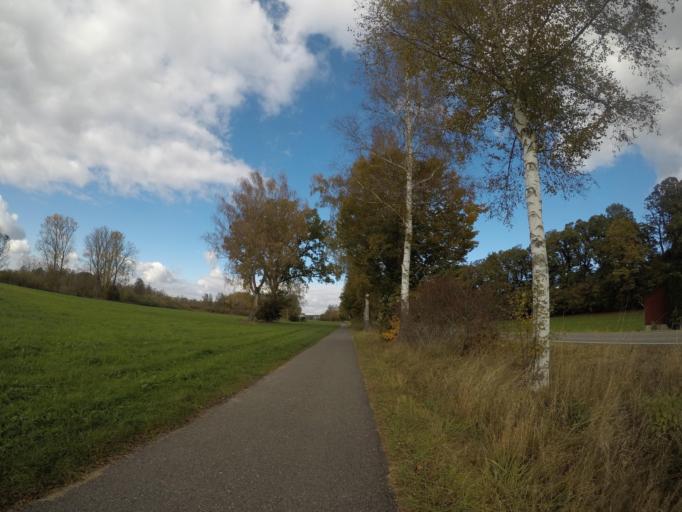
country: DE
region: Baden-Wuerttemberg
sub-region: Tuebingen Region
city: Seekirch
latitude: 48.0945
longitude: 9.6500
